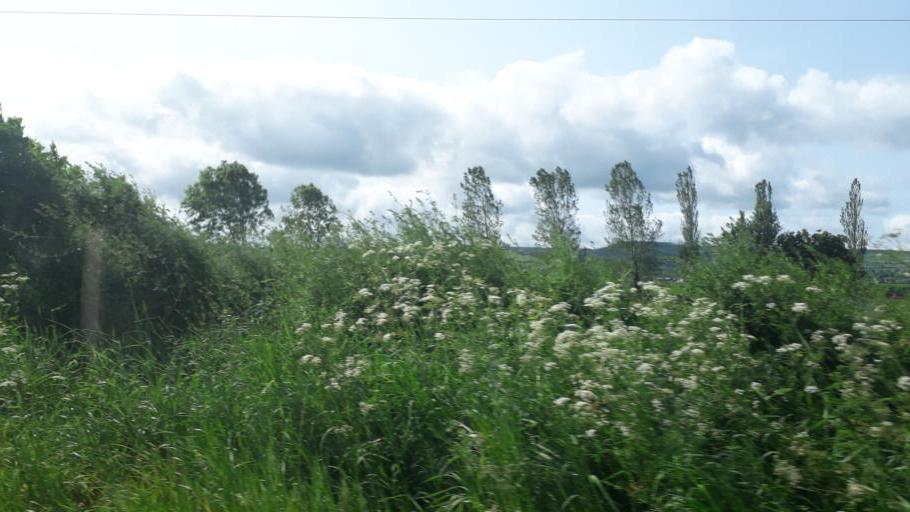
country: IE
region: Leinster
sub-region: Kilkenny
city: Graiguenamanagh
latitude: 52.6056
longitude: -7.0062
